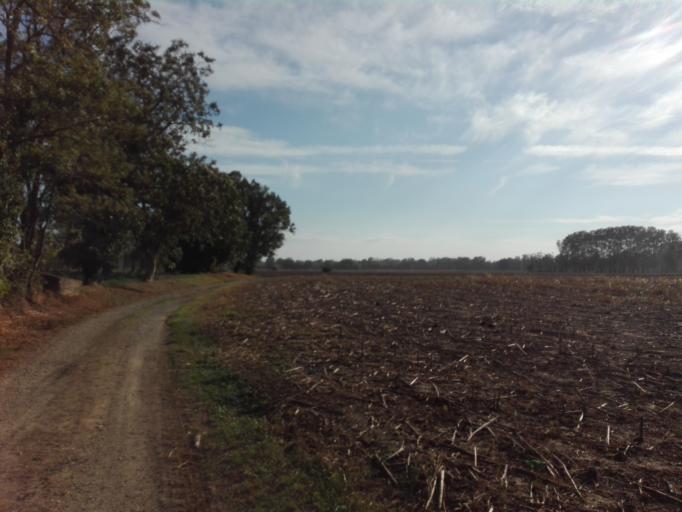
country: FR
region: Midi-Pyrenees
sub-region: Departement de la Haute-Garonne
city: Ondes
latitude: 43.7678
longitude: 1.3073
